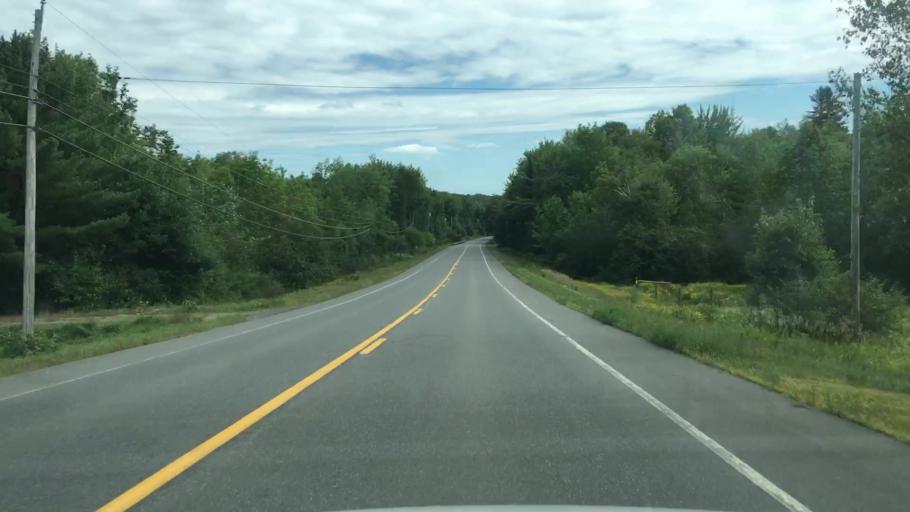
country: US
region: Maine
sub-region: Piscataquis County
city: Dover-Foxcroft
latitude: 45.2257
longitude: -69.1215
